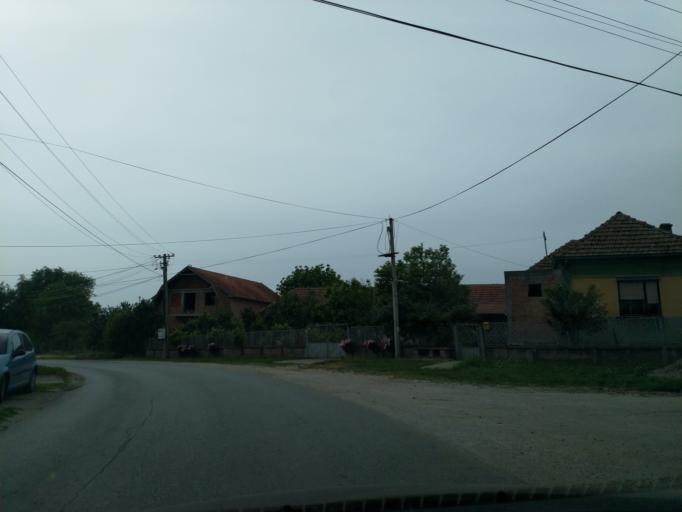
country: RS
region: Central Serbia
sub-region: Pomoravski Okrug
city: Jagodina
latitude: 43.9703
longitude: 21.2265
